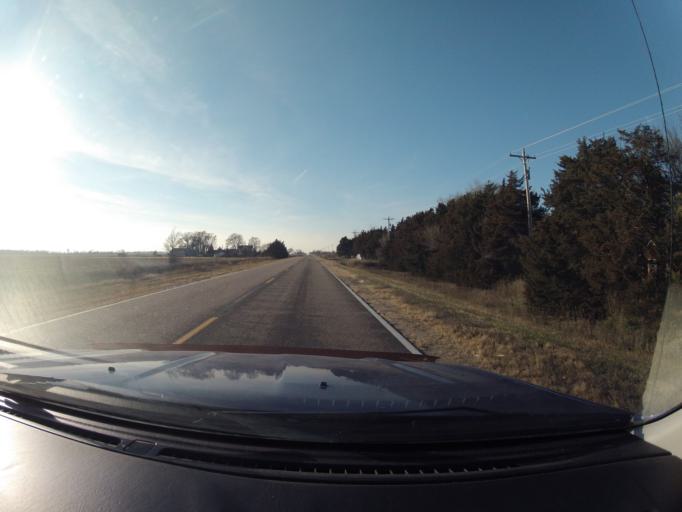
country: US
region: Nebraska
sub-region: Buffalo County
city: Kearney
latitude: 40.6410
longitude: -98.9636
